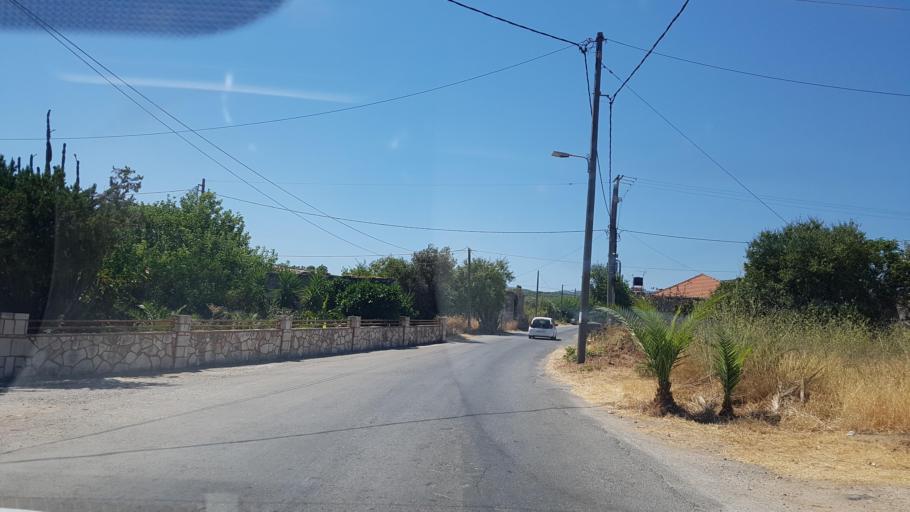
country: GR
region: Crete
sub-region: Nomos Chanias
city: Kissamos
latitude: 35.4921
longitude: 23.6844
